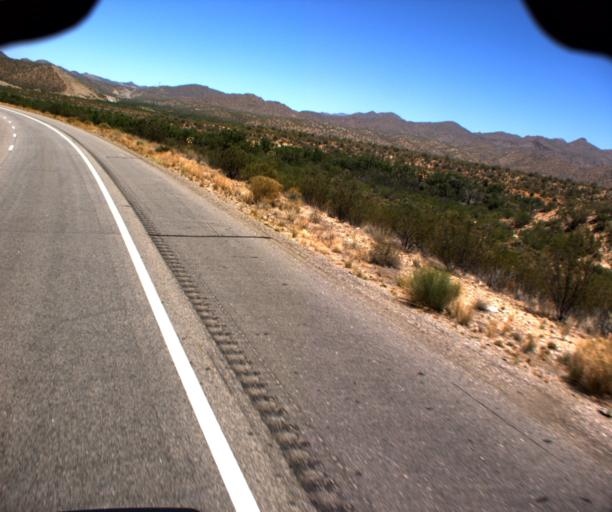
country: US
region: Arizona
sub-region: Yavapai County
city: Bagdad
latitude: 34.3668
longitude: -113.1776
